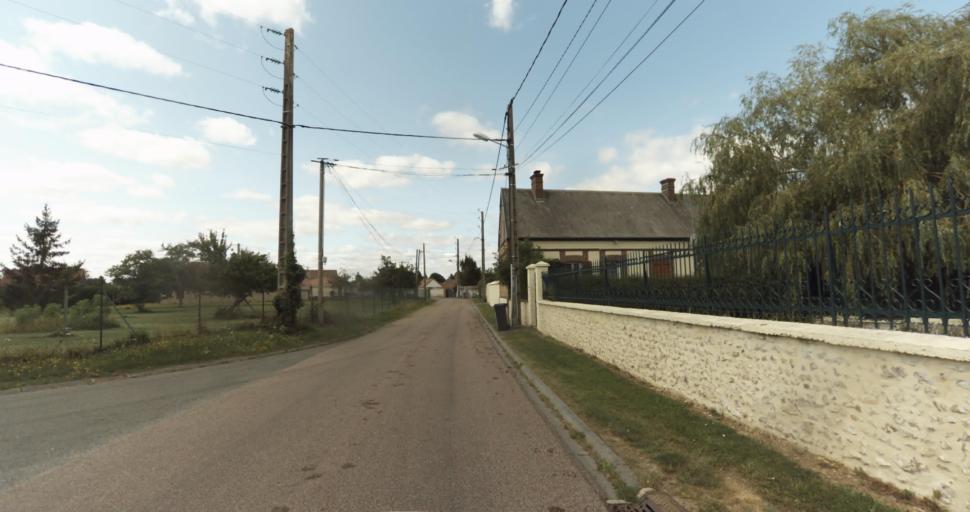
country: FR
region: Haute-Normandie
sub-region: Departement de l'Eure
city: La Madeleine-de-Nonancourt
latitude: 48.8281
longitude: 1.1785
